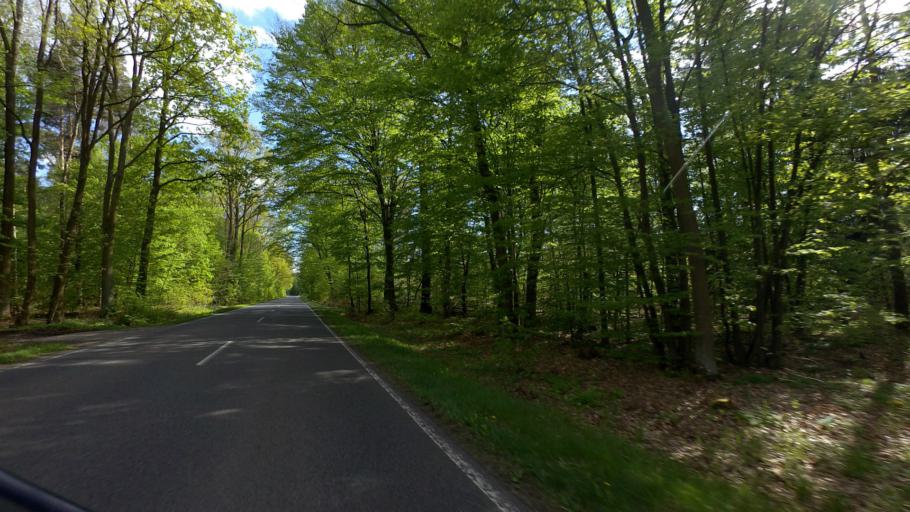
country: DE
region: Brandenburg
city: Liebenwalde
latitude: 52.8228
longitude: 13.4092
